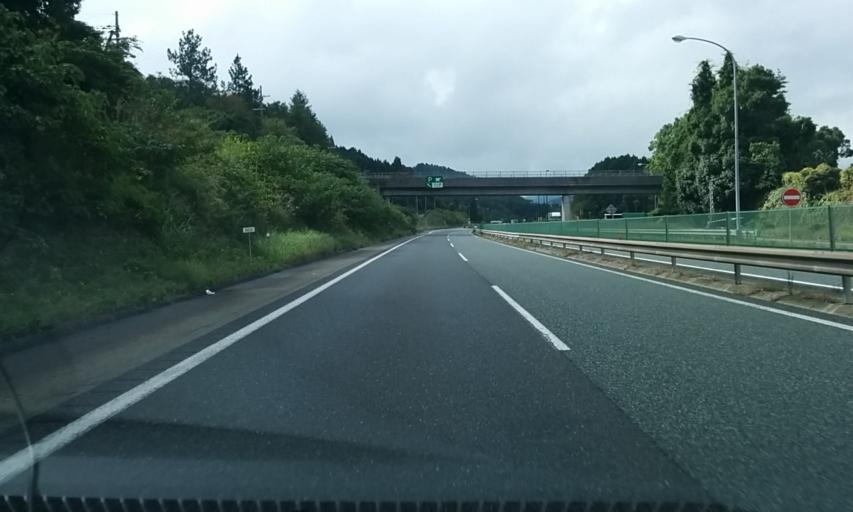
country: JP
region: Kyoto
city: Fukuchiyama
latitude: 35.2601
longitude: 135.1832
